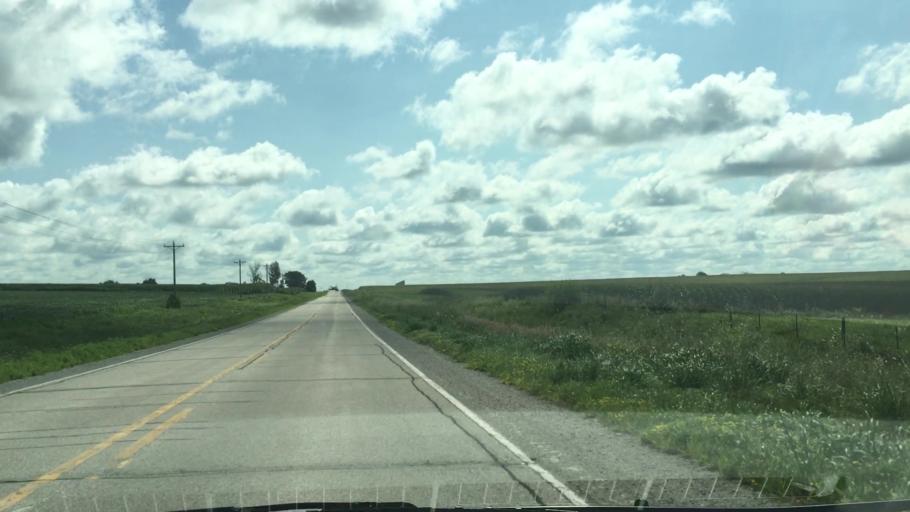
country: US
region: Iowa
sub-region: Johnson County
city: Solon
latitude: 41.8310
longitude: -91.4524
